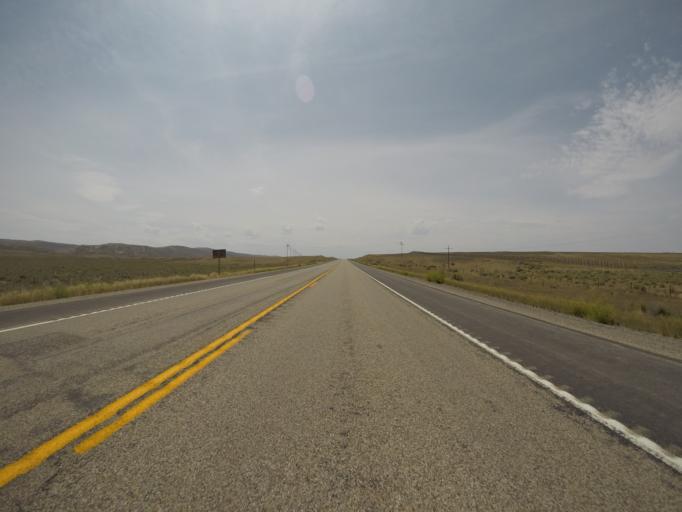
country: US
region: Wyoming
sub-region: Lincoln County
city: Kemmerer
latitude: 41.7016
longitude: -110.5661
